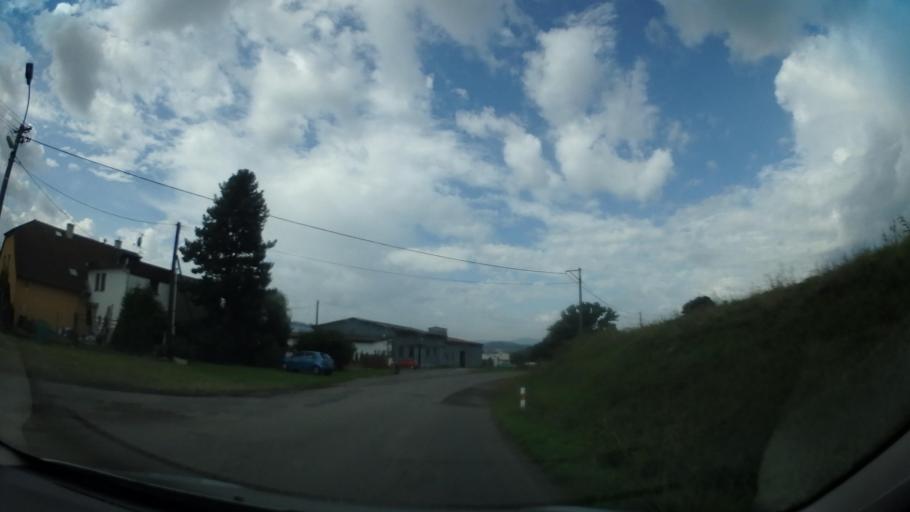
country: CZ
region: Plzensky
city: Horazd'ovice
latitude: 49.2616
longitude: 13.6707
